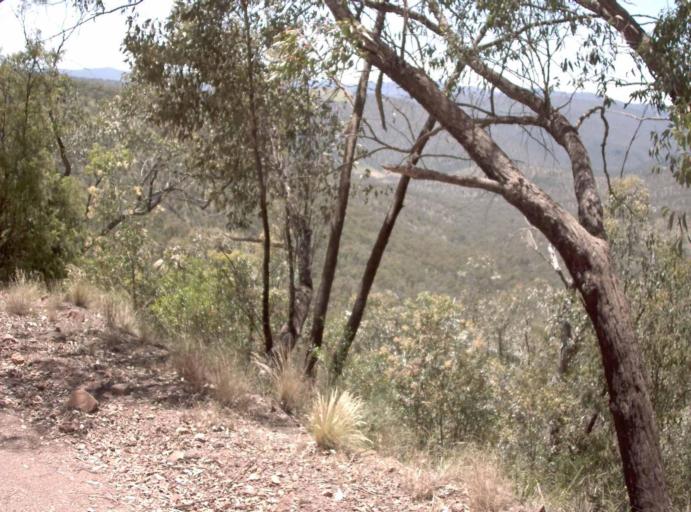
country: AU
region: New South Wales
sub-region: Snowy River
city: Jindabyne
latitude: -36.9866
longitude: 148.3004
